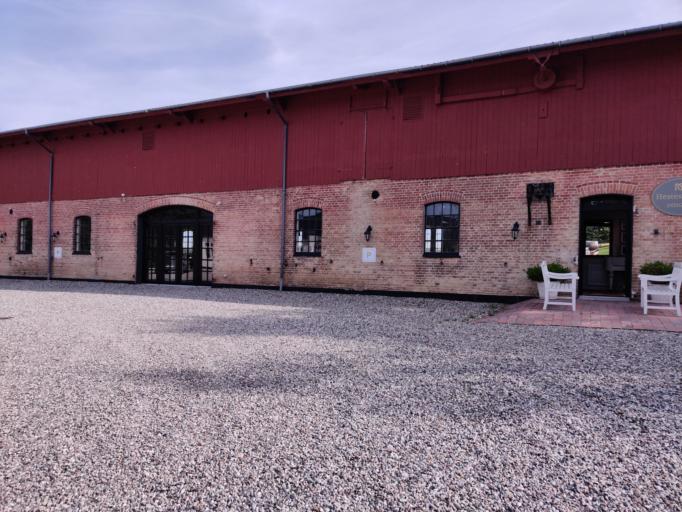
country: DK
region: Zealand
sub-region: Guldborgsund Kommune
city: Nykobing Falster
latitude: 54.6387
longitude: 11.8939
